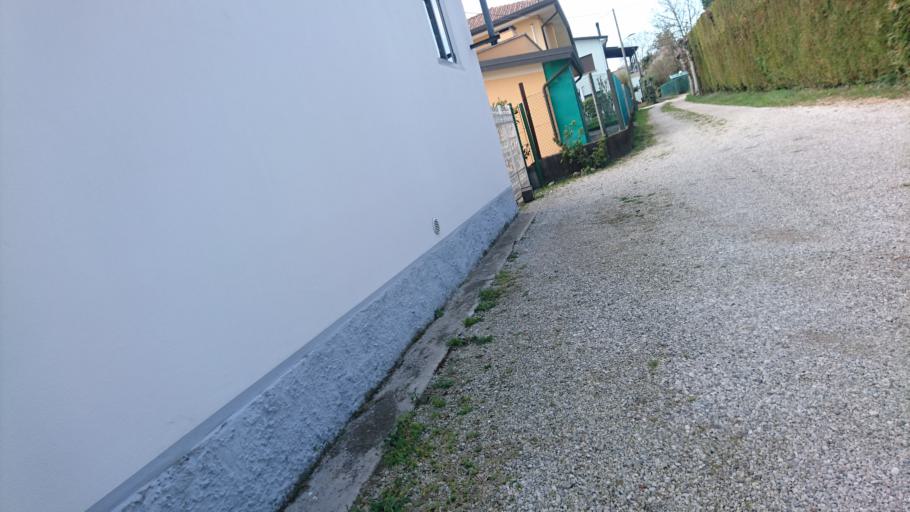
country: IT
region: Veneto
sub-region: Provincia di Padova
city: Padova
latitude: 45.3825
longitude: 11.8860
